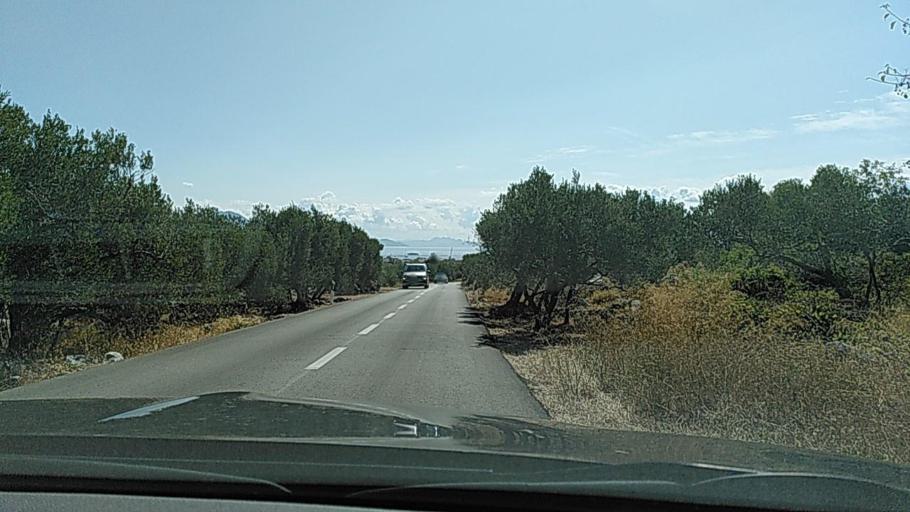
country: HR
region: Dubrovacko-Neretvanska
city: Orebic
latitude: 43.1309
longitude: 17.1732
